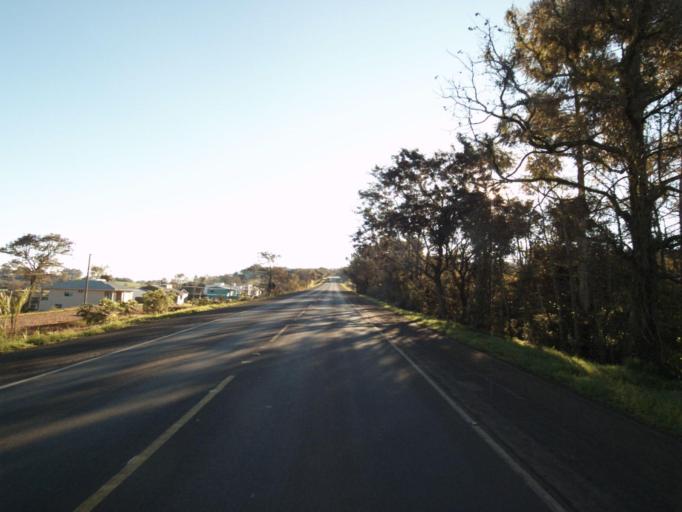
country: BR
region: Santa Catarina
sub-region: Chapeco
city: Chapeco
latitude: -26.9044
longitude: -52.9078
